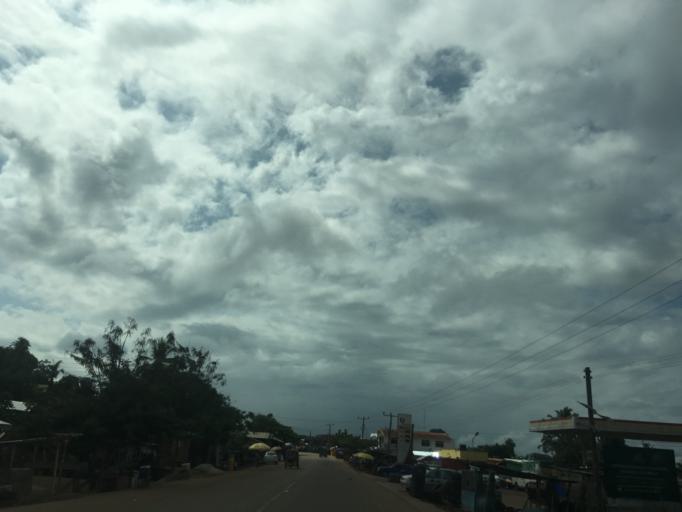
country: GH
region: Western
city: Wassa-Akropong
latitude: 5.8046
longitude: -2.4320
